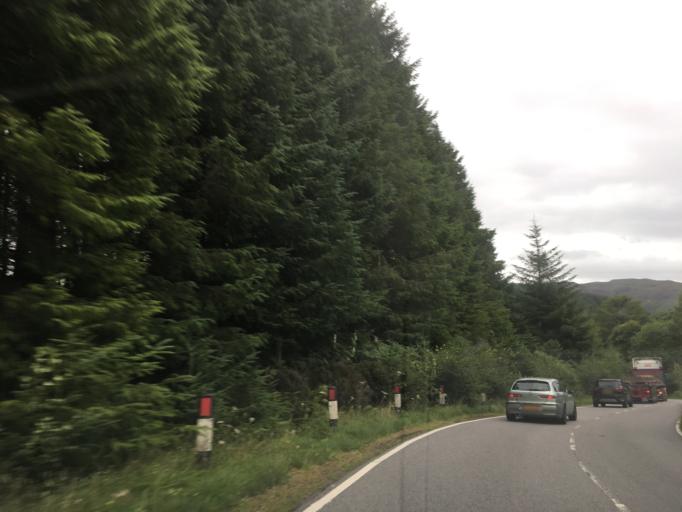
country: GB
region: Scotland
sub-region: Argyll and Bute
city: Oban
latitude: 56.2770
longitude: -5.4800
